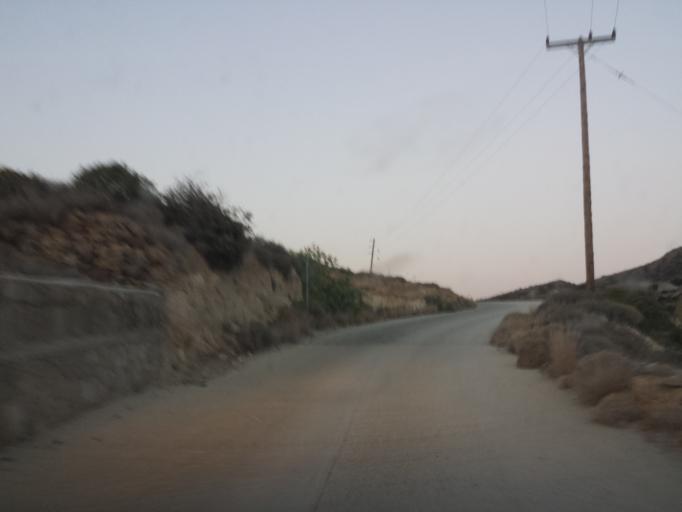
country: GR
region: South Aegean
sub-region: Nomos Kykladon
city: Milos
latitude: 36.7510
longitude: 24.4169
